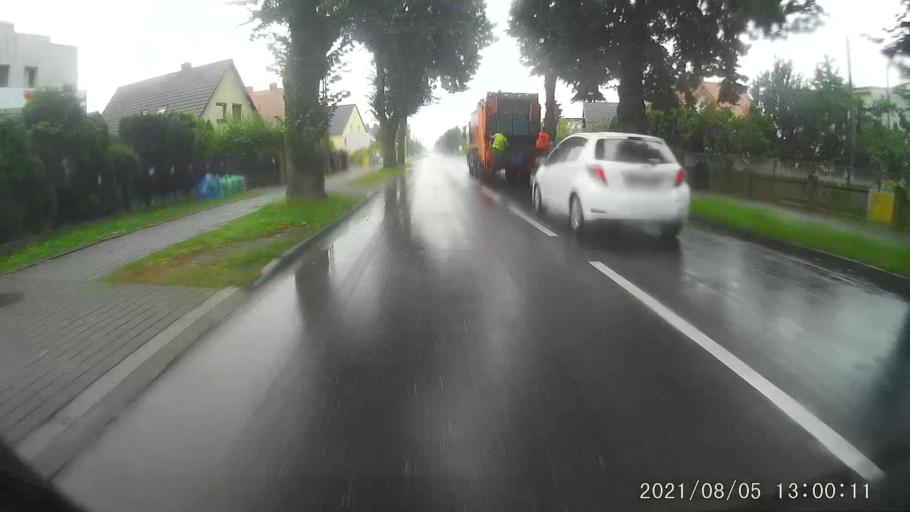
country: PL
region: Opole Voivodeship
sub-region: Powiat krapkowicki
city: Krapkowice
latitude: 50.4800
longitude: 17.9838
